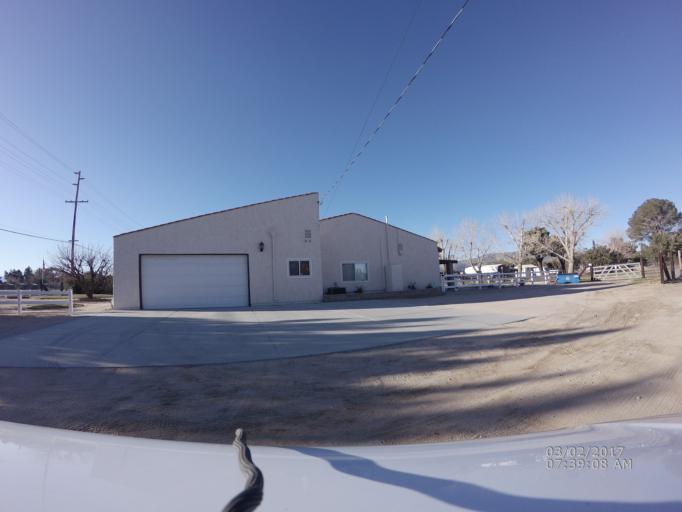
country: US
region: California
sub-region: Los Angeles County
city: Desert View Highlands
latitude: 34.6200
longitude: -118.1659
